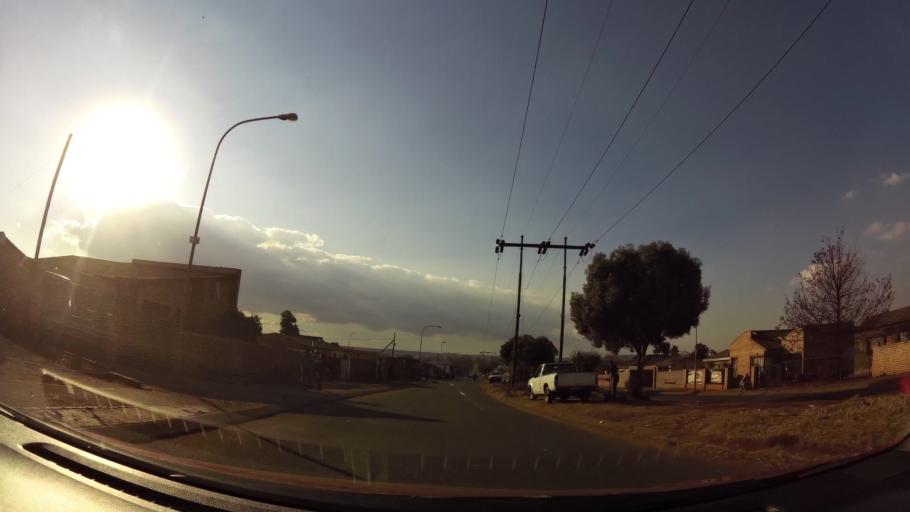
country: ZA
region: Gauteng
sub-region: City of Johannesburg Metropolitan Municipality
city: Soweto
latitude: -26.2275
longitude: 27.8581
